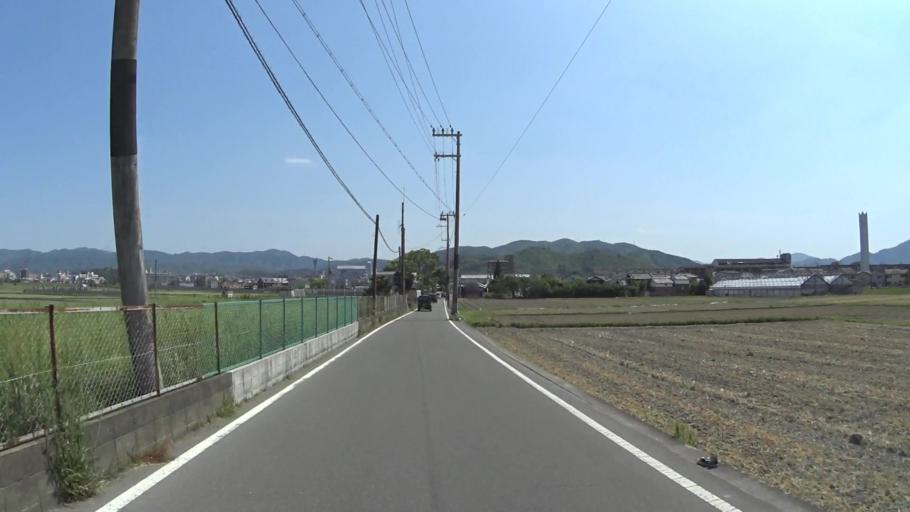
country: JP
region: Kyoto
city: Kameoka
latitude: 35.0254
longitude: 135.5709
